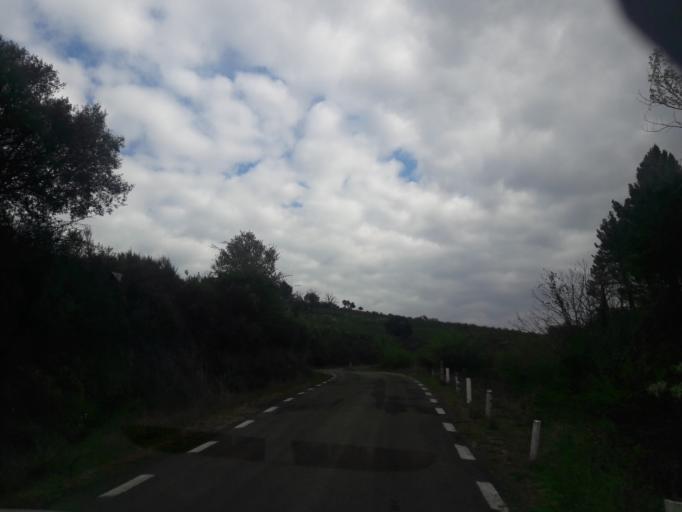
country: ES
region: Castille and Leon
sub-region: Provincia de Salamanca
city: Serradilla del Arroyo
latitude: 40.5093
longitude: -6.3988
